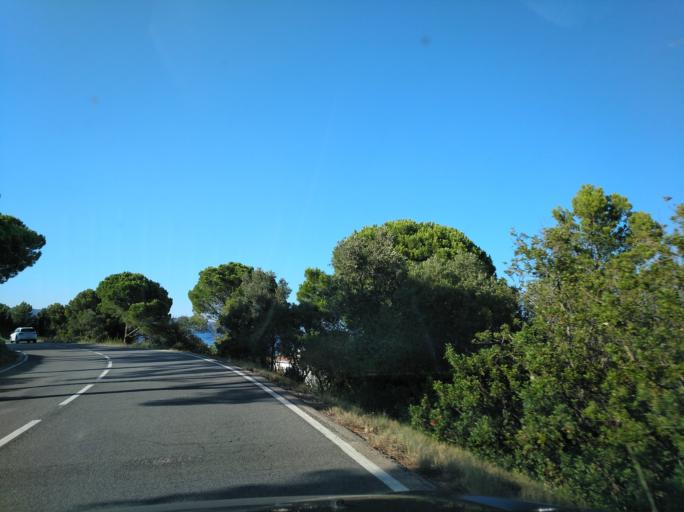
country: ES
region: Catalonia
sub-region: Provincia de Girona
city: Llanca
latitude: 42.3514
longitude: 3.1765
